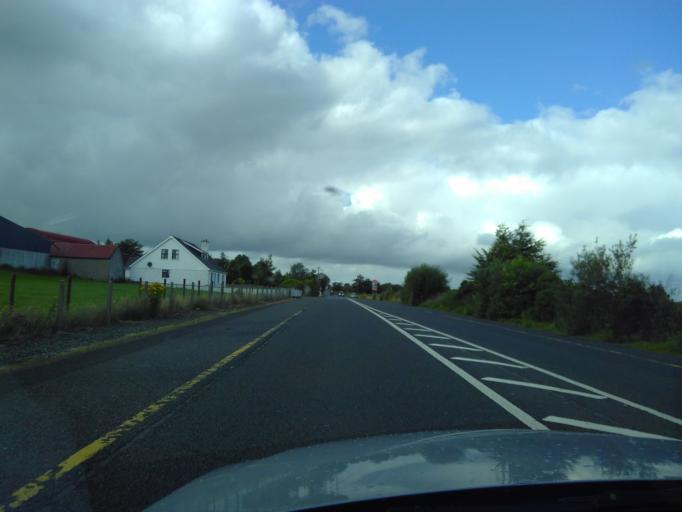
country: IE
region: Ulster
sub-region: County Donegal
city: Ramelton
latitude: 54.9933
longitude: -7.6637
